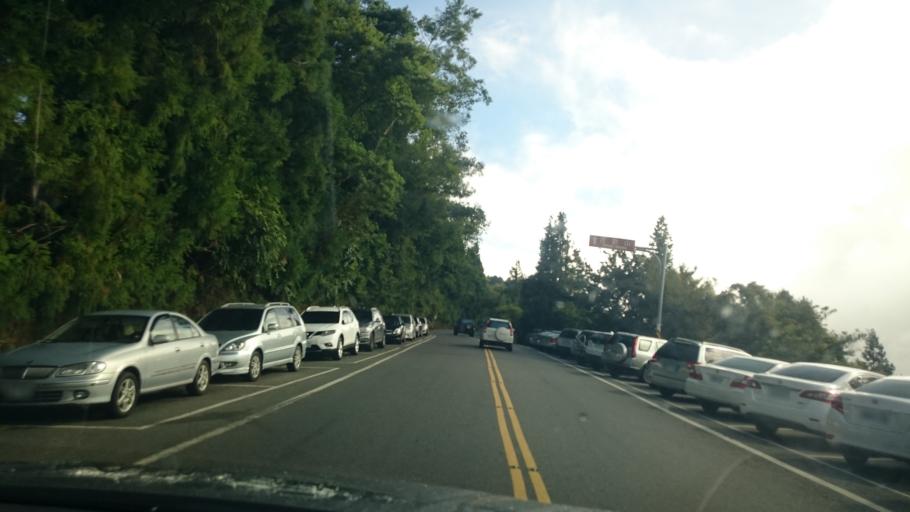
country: TW
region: Taiwan
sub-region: Nantou
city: Puli
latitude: 24.0554
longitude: 121.1624
